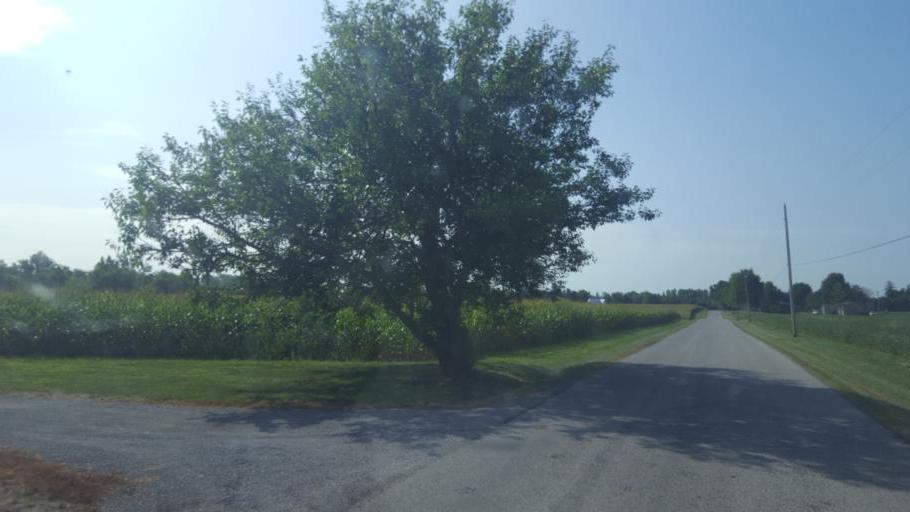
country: US
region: Ohio
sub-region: Morrow County
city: Cardington
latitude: 40.5055
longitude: -82.9196
